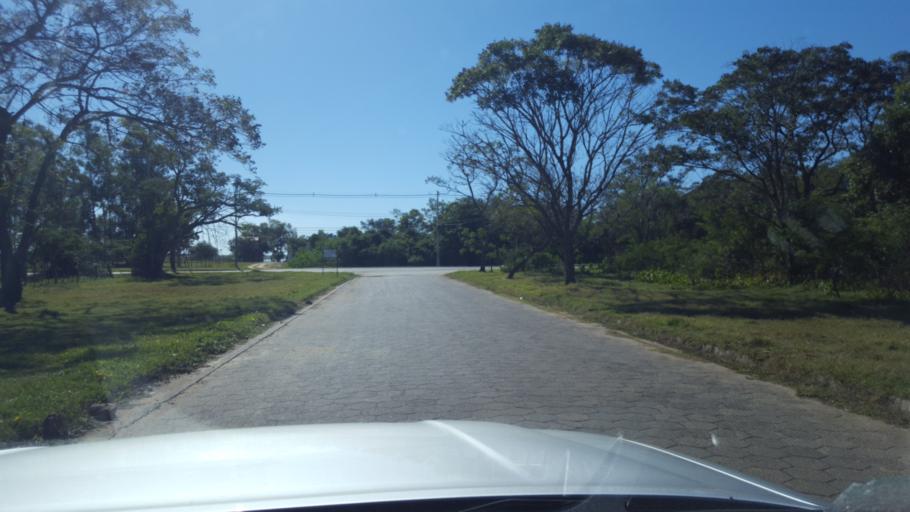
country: PY
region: Neembucu
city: Pilar
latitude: -26.8702
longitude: -58.3179
